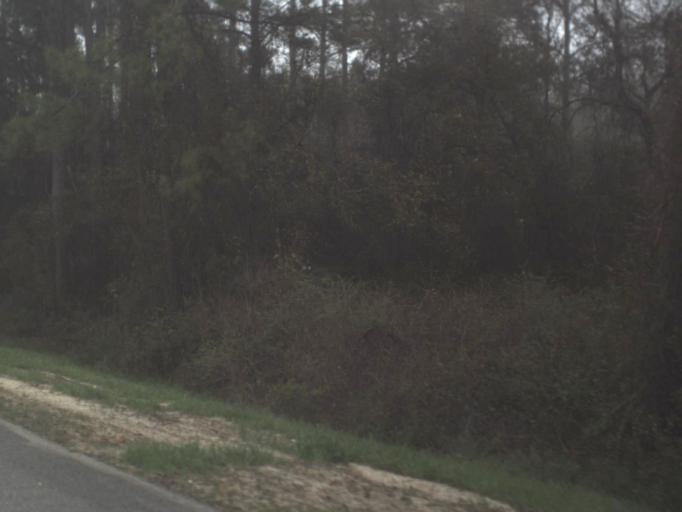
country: US
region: Florida
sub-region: Gadsden County
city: Gretna
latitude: 30.4875
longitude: -84.7221
